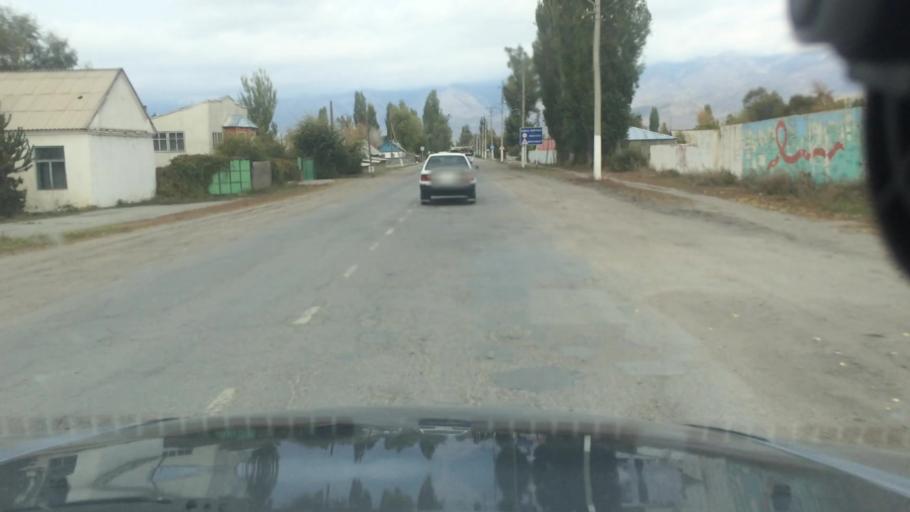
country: KG
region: Ysyk-Koel
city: Tyup
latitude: 42.7228
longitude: 78.3667
